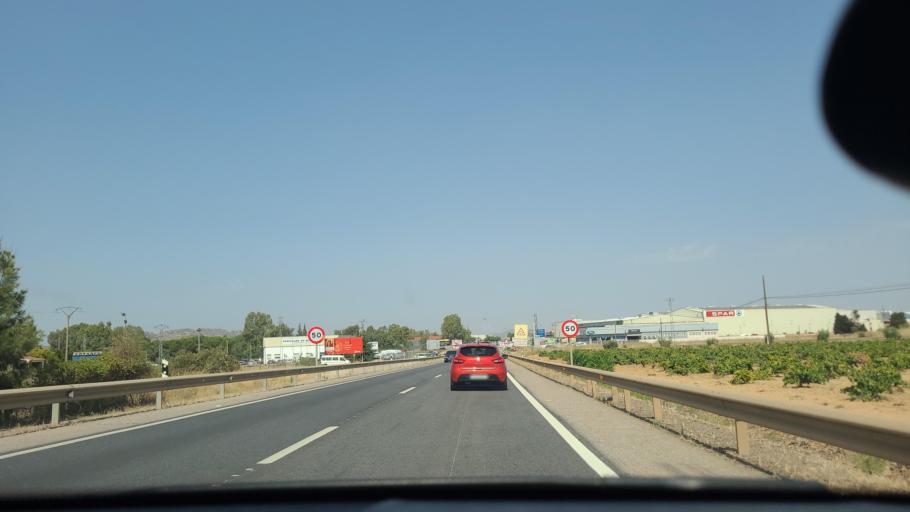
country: ES
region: Extremadura
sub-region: Provincia de Badajoz
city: Puebla de Sancho Perez
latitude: 38.4127
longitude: -6.3952
